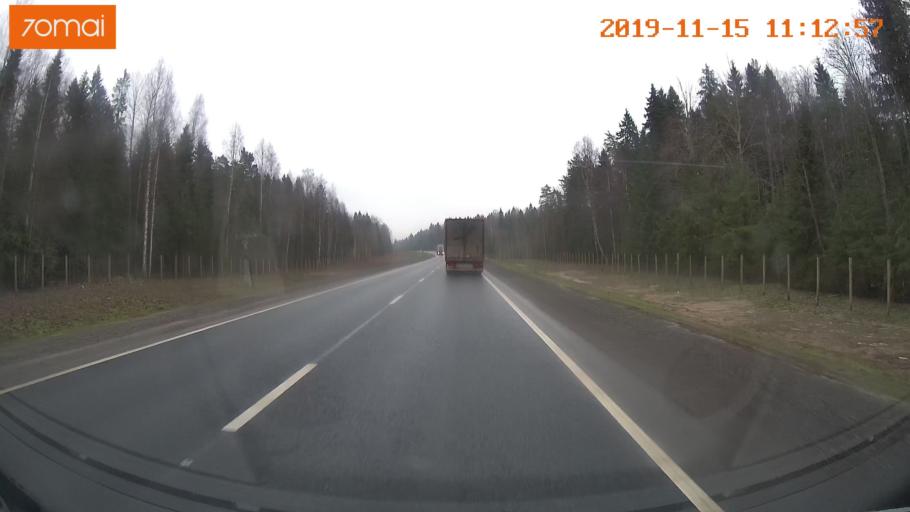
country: RU
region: Vologda
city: Chebsara
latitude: 59.1216
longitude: 39.1591
